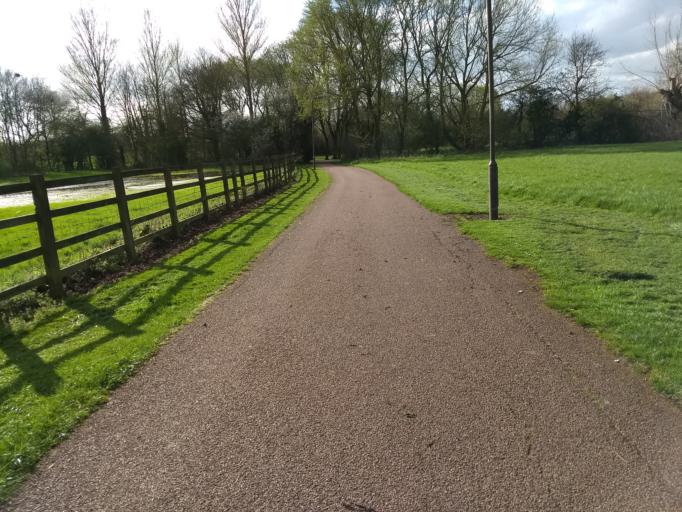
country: GB
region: England
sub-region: Milton Keynes
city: Simpson
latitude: 52.0237
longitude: -0.7146
